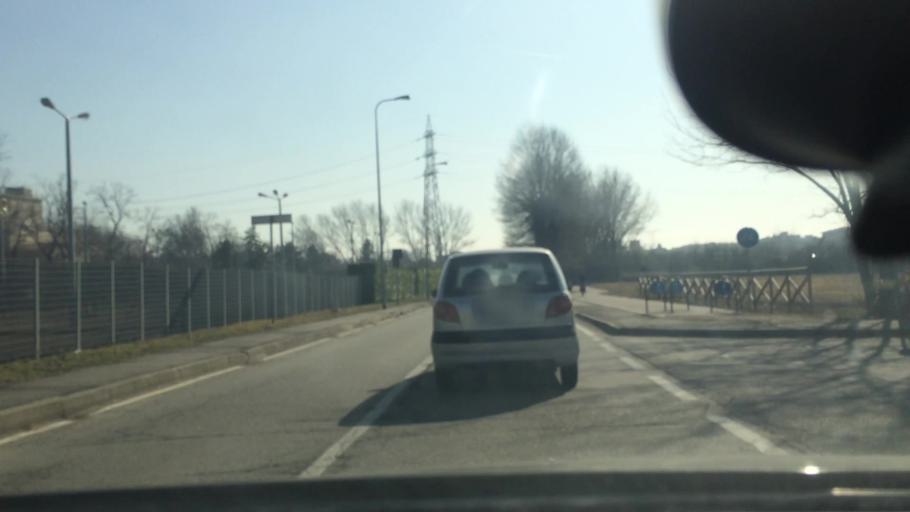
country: IT
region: Lombardy
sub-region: Provincia di Monza e Brianza
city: Ceriano Laghetto
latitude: 45.6245
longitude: 9.0804
